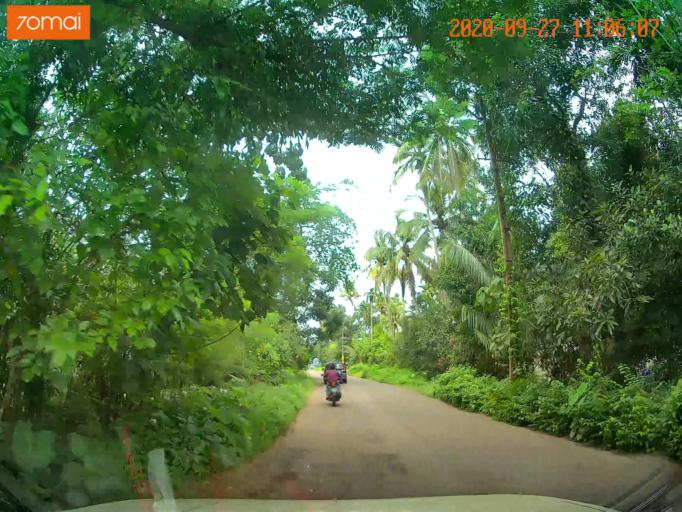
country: IN
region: Kerala
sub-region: Thrissur District
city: Irinjalakuda
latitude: 10.4246
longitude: 76.2444
